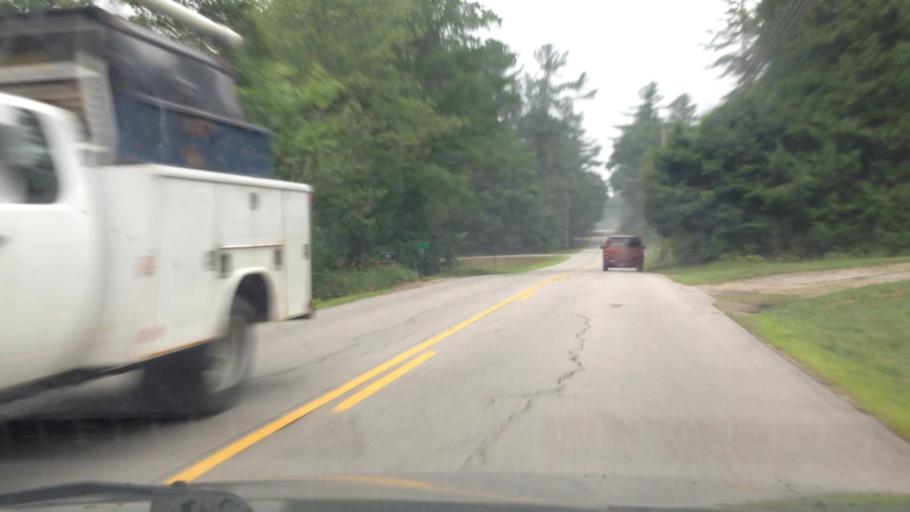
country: US
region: New Hampshire
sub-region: Cheshire County
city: Swanzey
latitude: 42.8642
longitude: -72.2435
